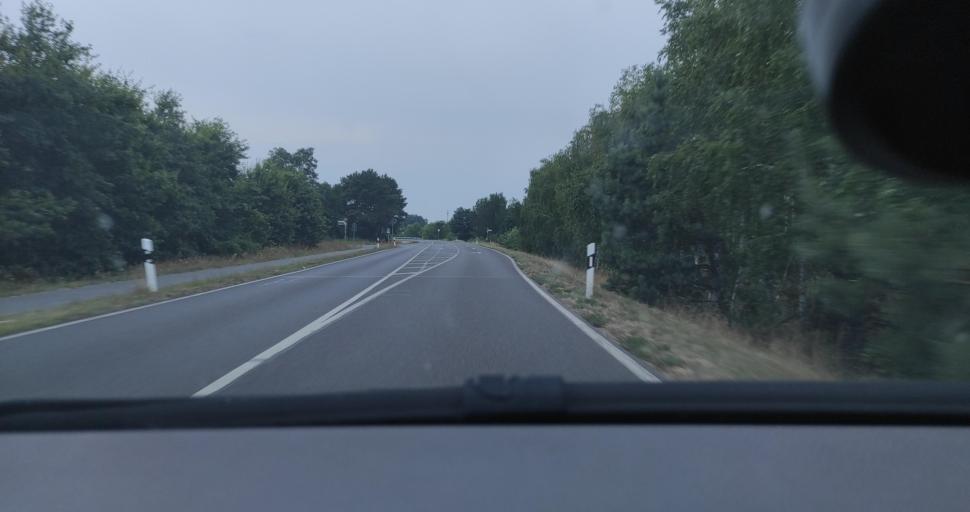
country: DE
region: Brandenburg
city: Forst
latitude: 51.7682
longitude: 14.6363
